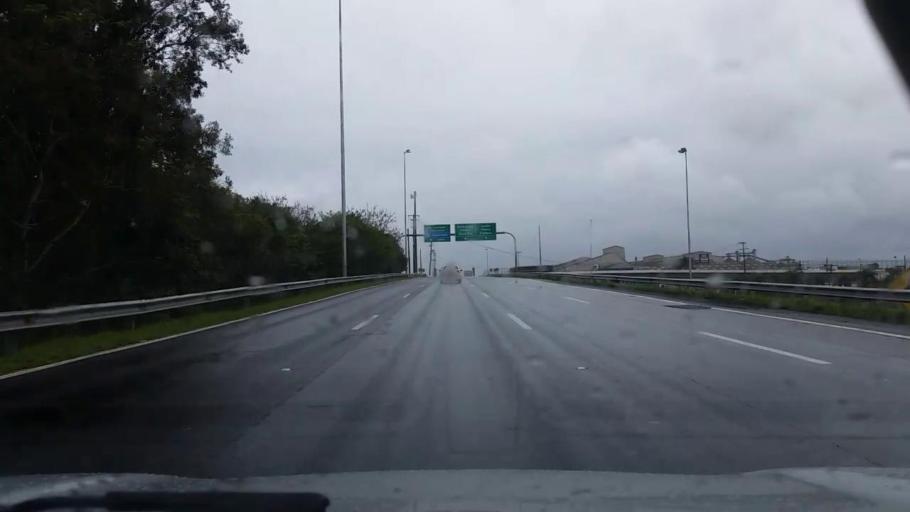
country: BR
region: Rio Grande do Sul
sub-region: Canoas
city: Canoas
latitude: -29.9694
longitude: -51.1738
